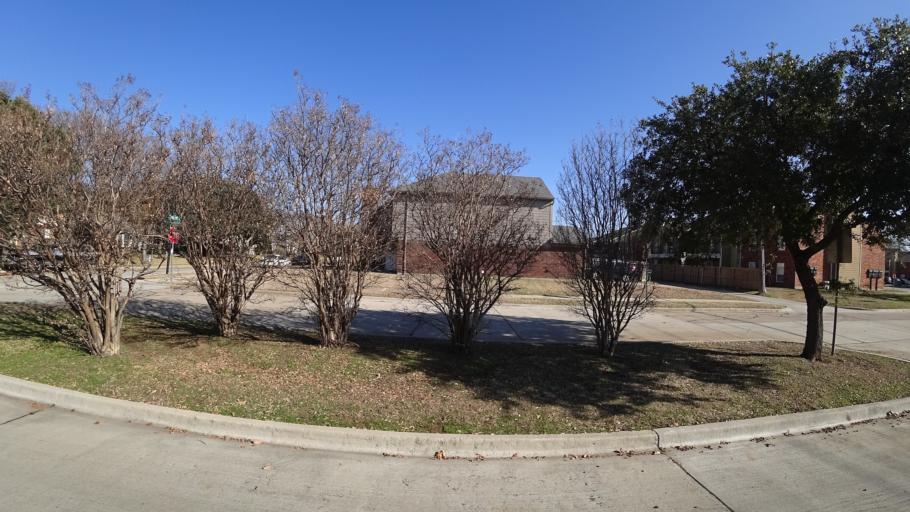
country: US
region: Texas
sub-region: Denton County
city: Lewisville
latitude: 33.0066
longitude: -97.0017
